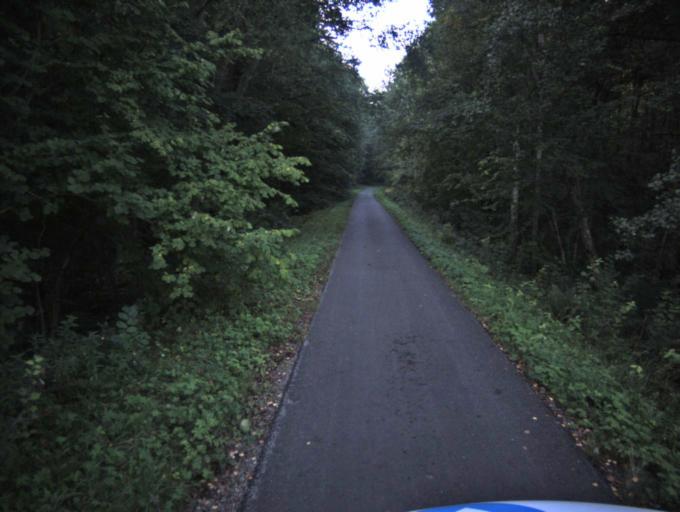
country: SE
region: Vaestra Goetaland
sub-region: Ulricehamns Kommun
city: Ulricehamn
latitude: 57.7301
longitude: 13.4097
